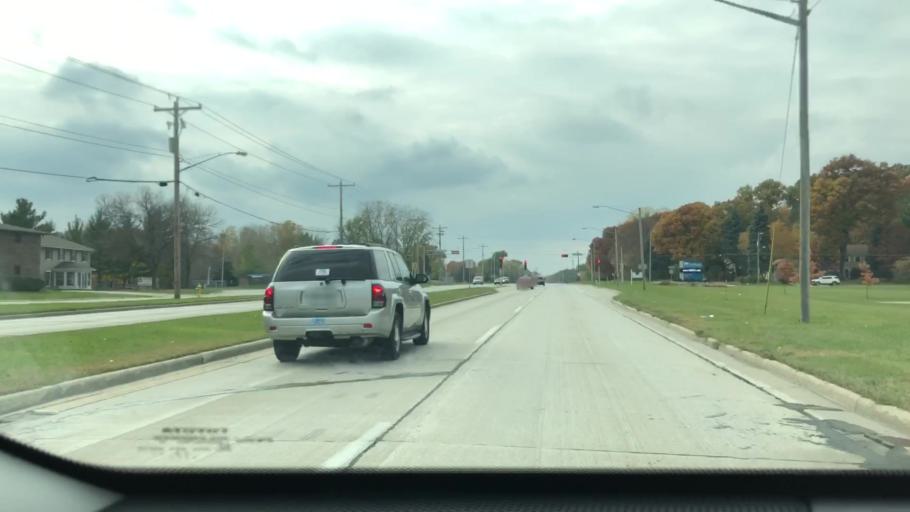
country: US
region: Wisconsin
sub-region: Brown County
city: Howard
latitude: 44.5240
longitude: -88.1076
